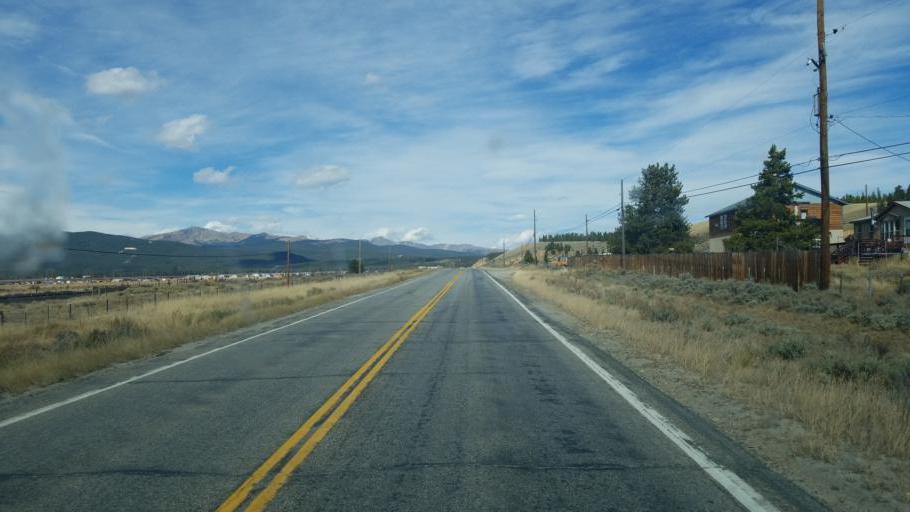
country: US
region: Colorado
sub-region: Lake County
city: Leadville North
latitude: 39.2111
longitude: -106.3460
